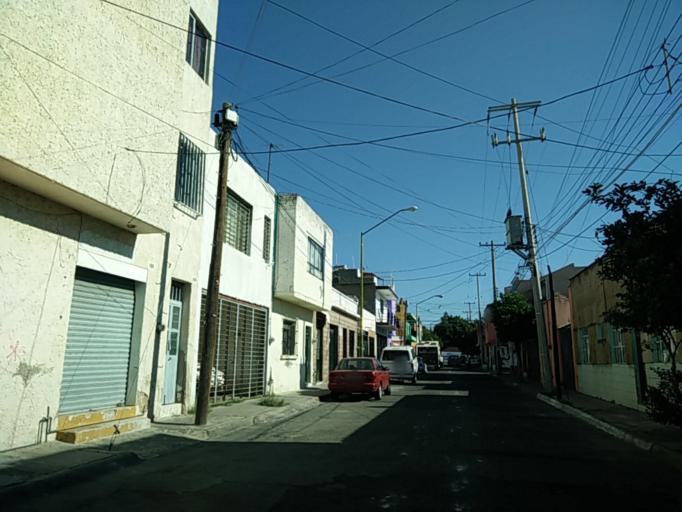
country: MX
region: Jalisco
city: Tlaquepaque
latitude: 20.6630
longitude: -103.3322
